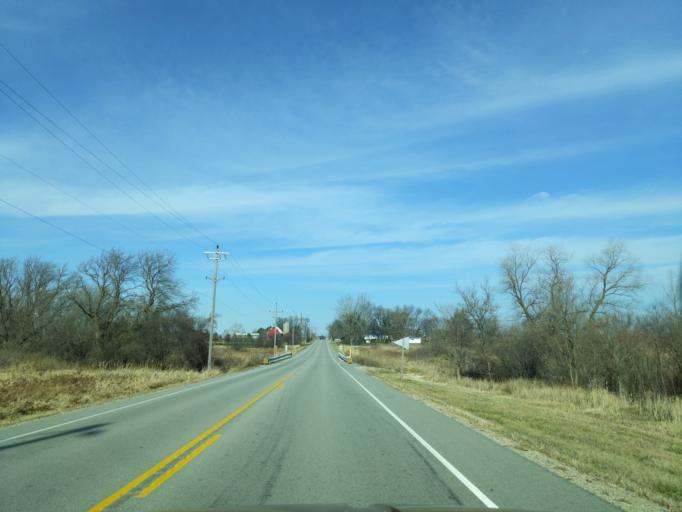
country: US
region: Wisconsin
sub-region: Walworth County
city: Elkhorn
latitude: 42.7114
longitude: -88.5817
